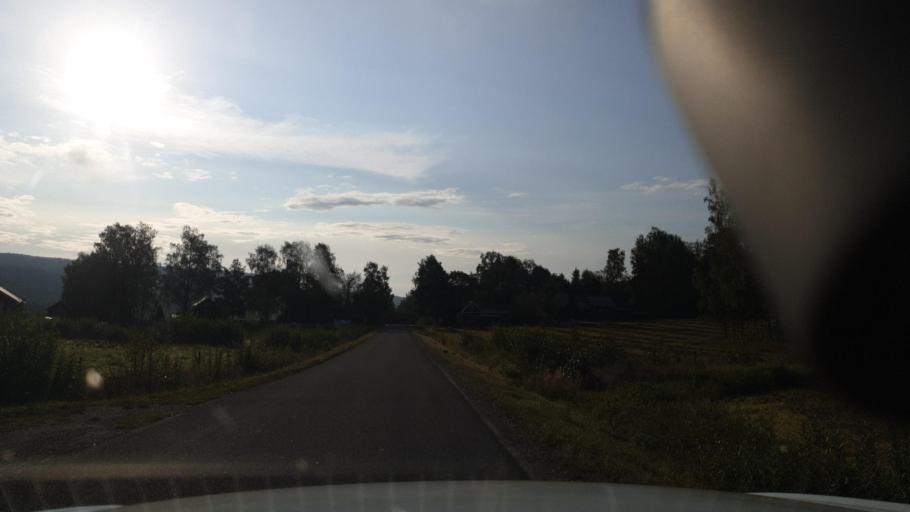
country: SE
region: Vaermland
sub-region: Arvika Kommun
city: Arvika
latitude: 59.7632
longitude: 12.5929
